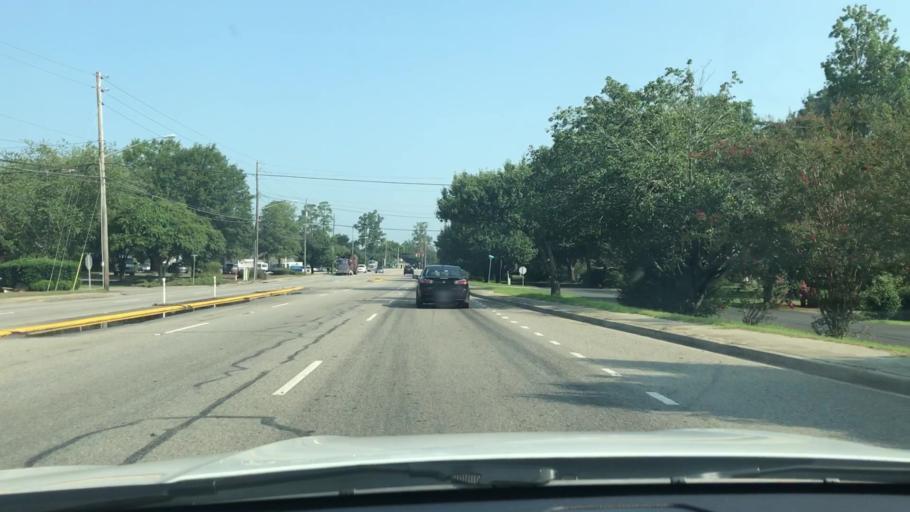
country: US
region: South Carolina
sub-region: Georgetown County
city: Georgetown
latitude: 33.3846
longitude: -79.2877
